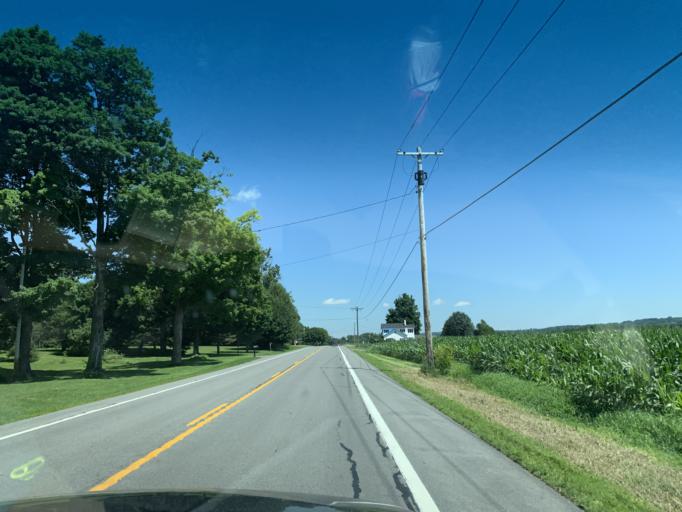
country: US
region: New York
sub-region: Oneida County
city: Chadwicks
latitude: 42.9040
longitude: -75.2420
